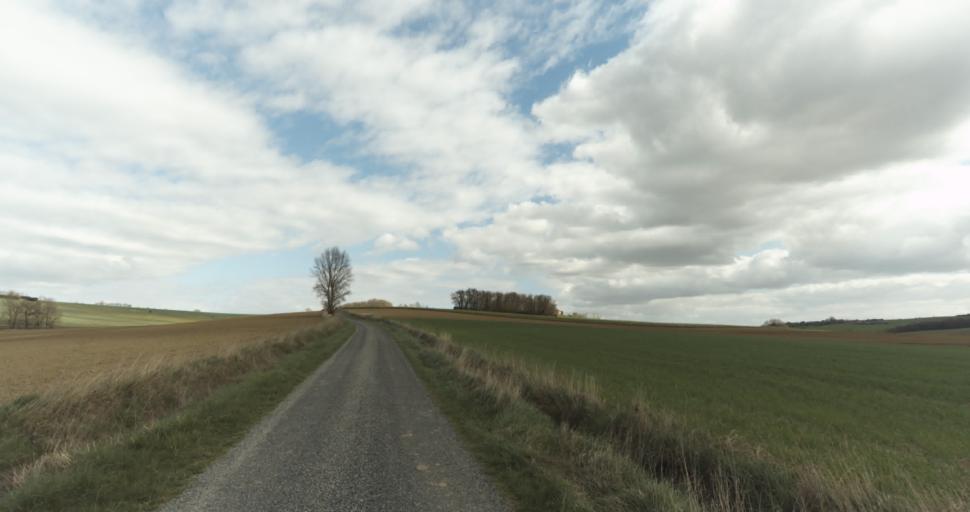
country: FR
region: Midi-Pyrenees
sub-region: Departement de la Haute-Garonne
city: Auterive
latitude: 43.3858
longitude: 1.4745
